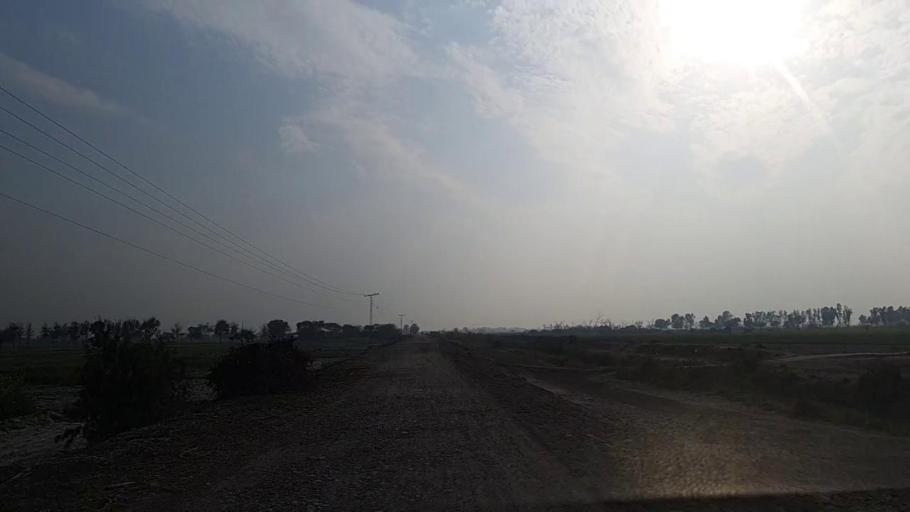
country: PK
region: Sindh
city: Jam Sahib
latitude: 26.3170
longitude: 68.5268
